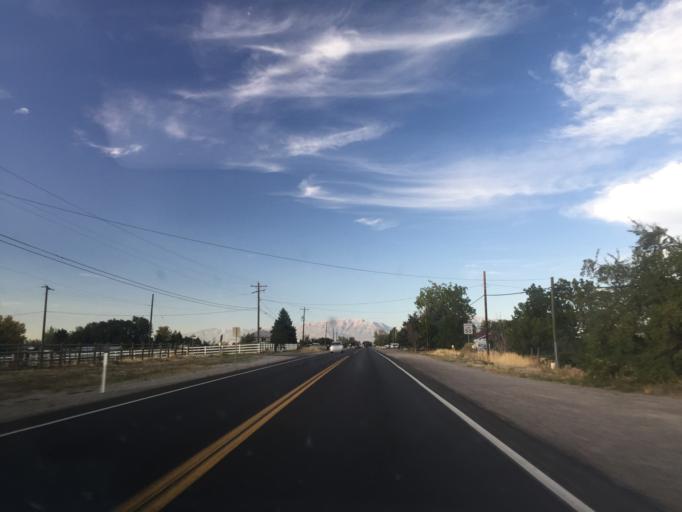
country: US
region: Utah
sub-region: Utah County
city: Payson
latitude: 40.0113
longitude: -111.7457
